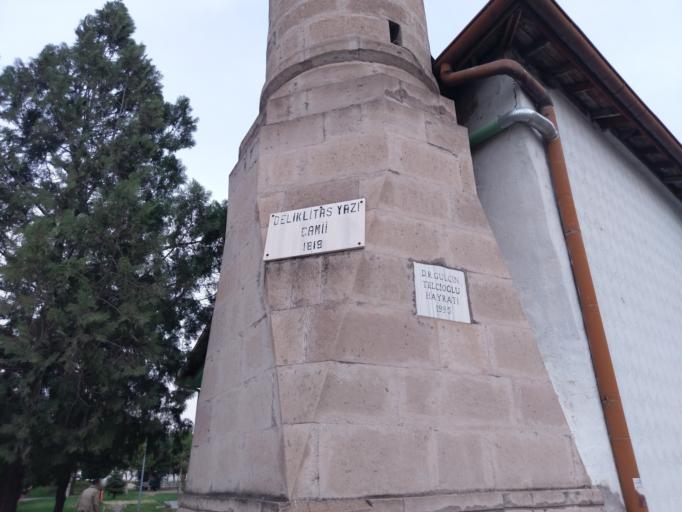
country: TR
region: Kayseri
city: Kayseri
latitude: 38.7119
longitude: 35.4900
